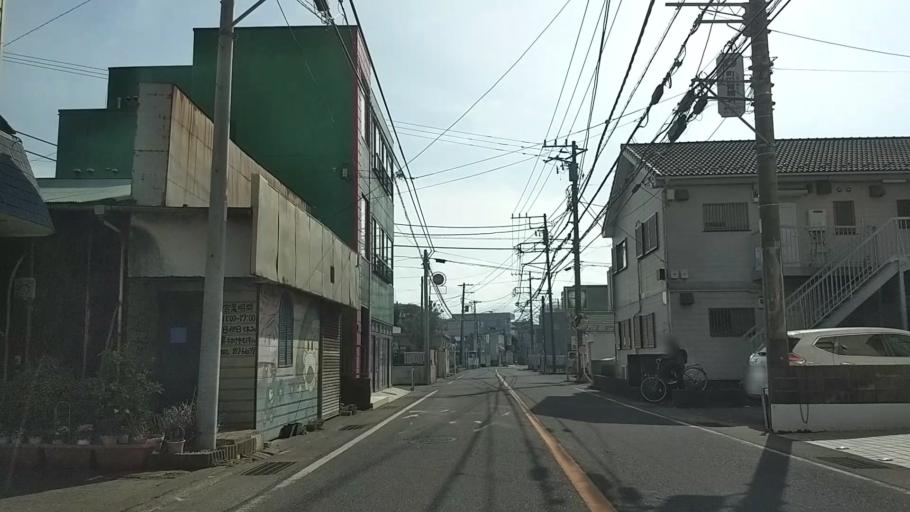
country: JP
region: Kanagawa
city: Chigasaki
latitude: 35.3370
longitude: 139.3829
